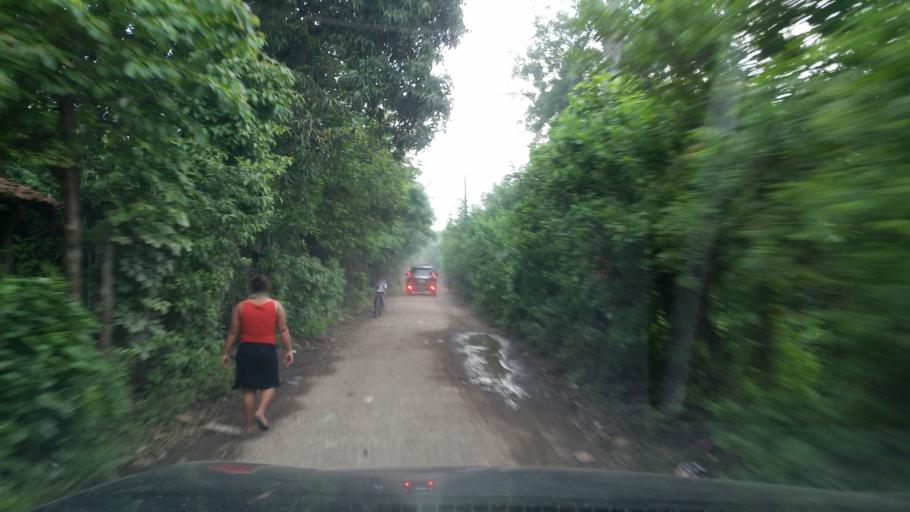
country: NI
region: Chinandega
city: Puerto Morazan
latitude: 12.7659
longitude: -87.1289
